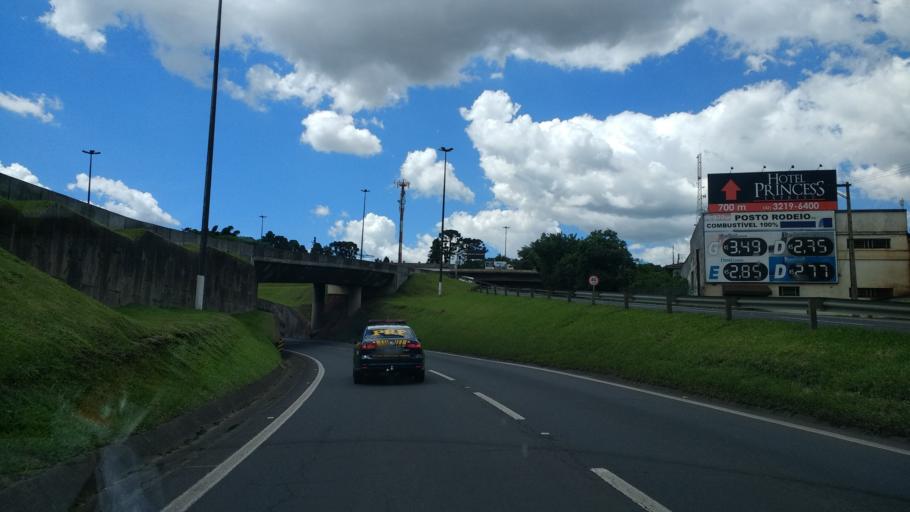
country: BR
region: Parana
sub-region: Ponta Grossa
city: Ponta Grossa
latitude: -25.0834
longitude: -50.1904
